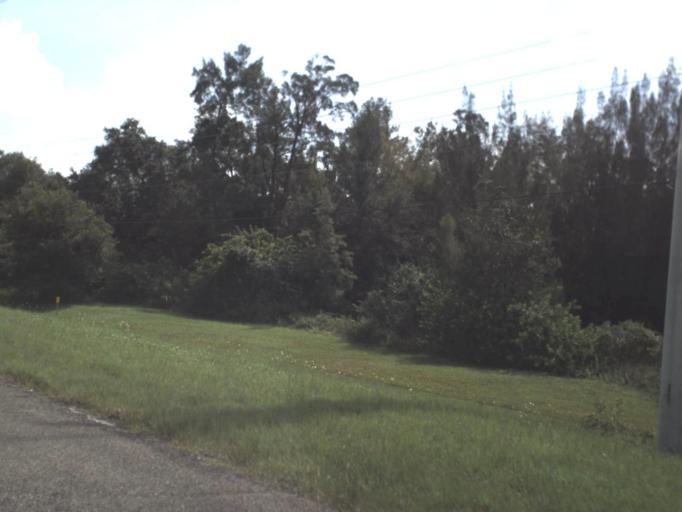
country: US
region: Florida
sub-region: Sarasota County
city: Warm Mineral Springs
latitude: 27.0422
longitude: -82.2981
